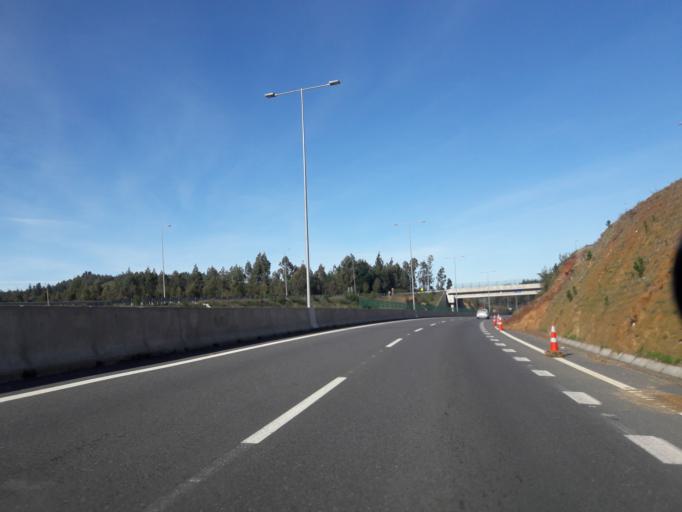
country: CL
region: Biobio
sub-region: Provincia de Biobio
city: Yumbel
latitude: -36.9333
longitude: -72.7625
